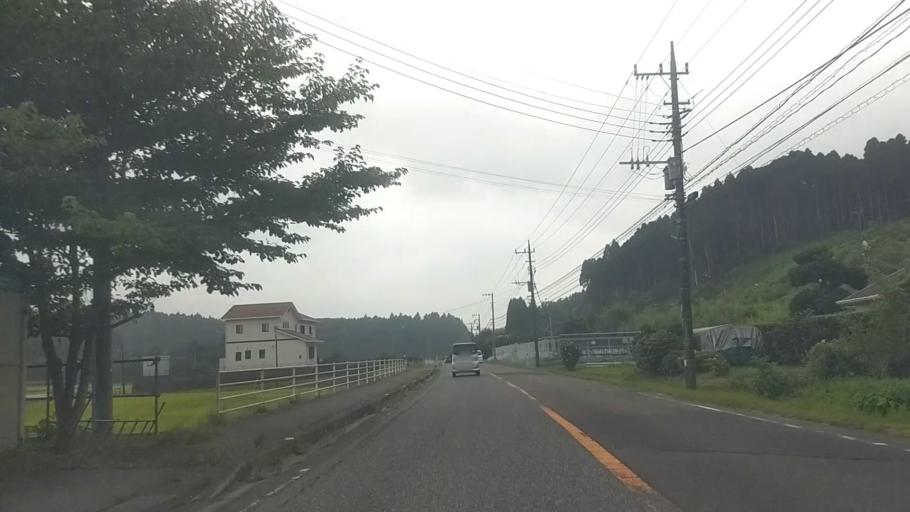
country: JP
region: Chiba
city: Ohara
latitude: 35.2731
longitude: 140.3306
